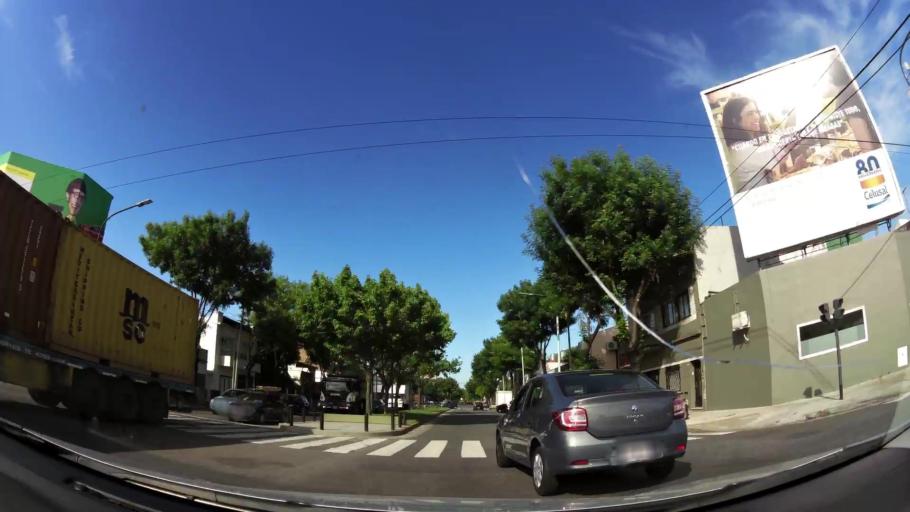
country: AR
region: Buenos Aires
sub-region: Partido de General San Martin
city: General San Martin
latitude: -34.5528
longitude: -58.4903
